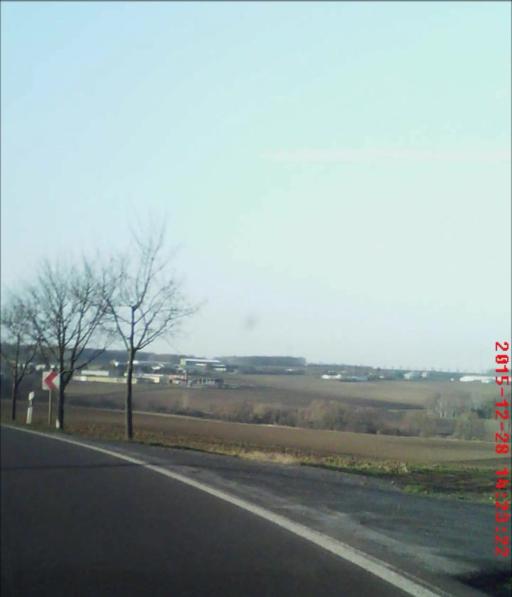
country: DE
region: Thuringia
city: Goldbach
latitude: 51.0541
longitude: 11.4612
